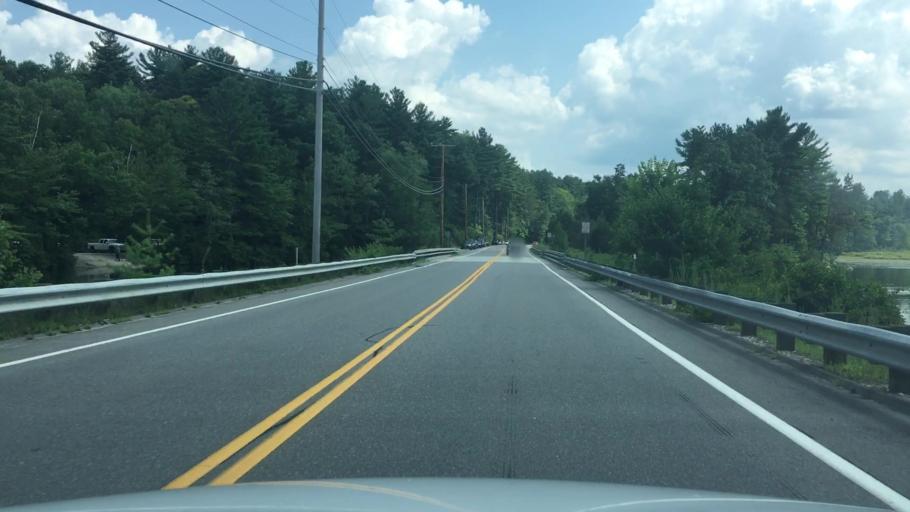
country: US
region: New Hampshire
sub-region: Rockingham County
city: Auburn
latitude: 42.9885
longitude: -71.3762
